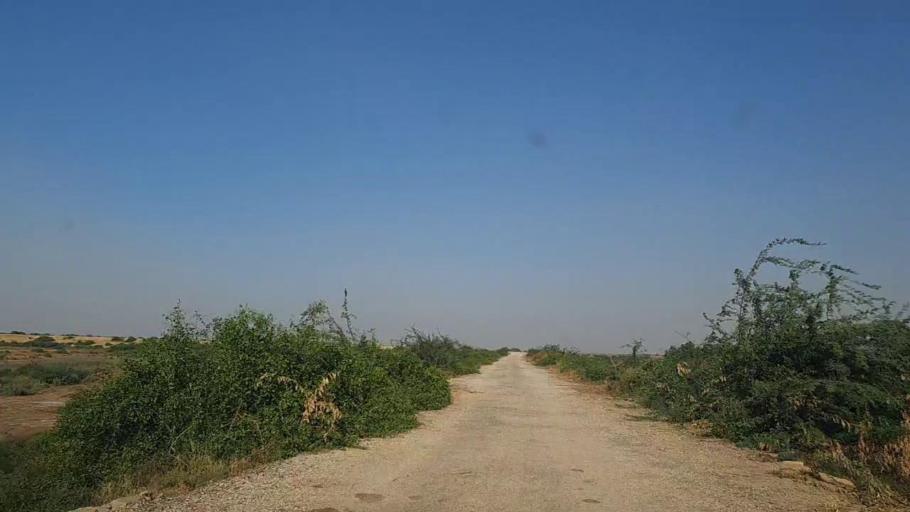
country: PK
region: Sindh
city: Daro Mehar
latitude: 25.0018
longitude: 68.1189
